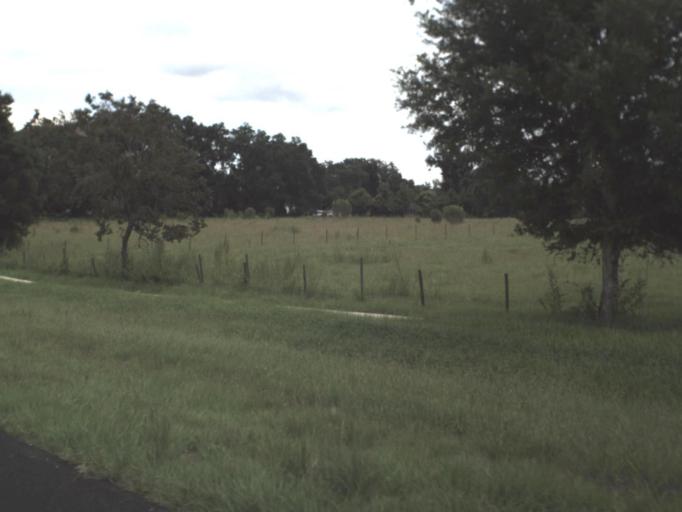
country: US
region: Florida
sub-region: Pasco County
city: Dade City North
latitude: 28.4219
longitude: -82.1905
